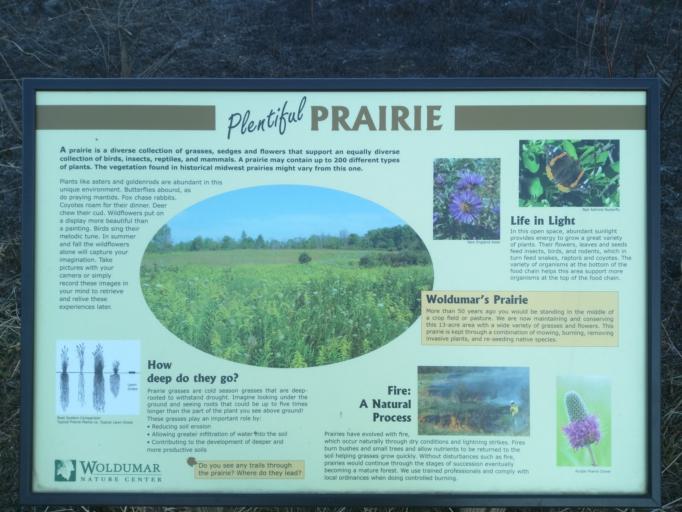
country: US
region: Michigan
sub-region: Eaton County
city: Dimondale
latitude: 42.6885
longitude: -84.6337
